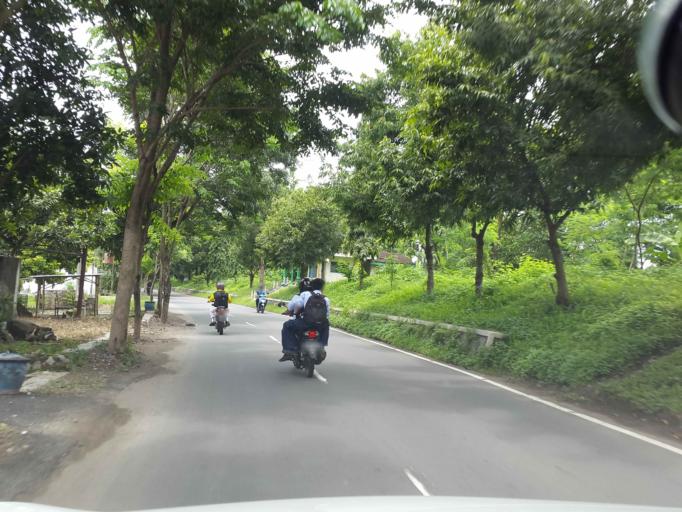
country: ID
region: East Java
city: Mojokerto
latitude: -7.4588
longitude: 112.4257
